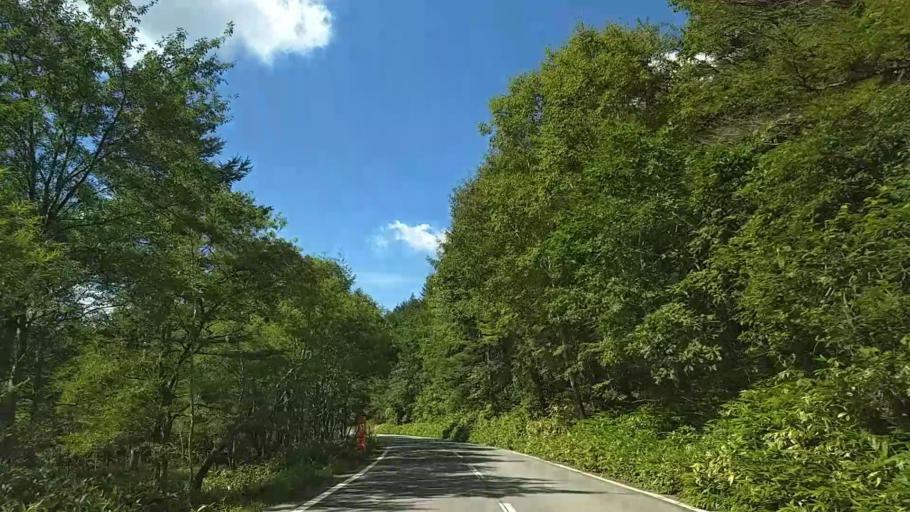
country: JP
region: Nagano
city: Chino
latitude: 36.0891
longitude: 138.2774
